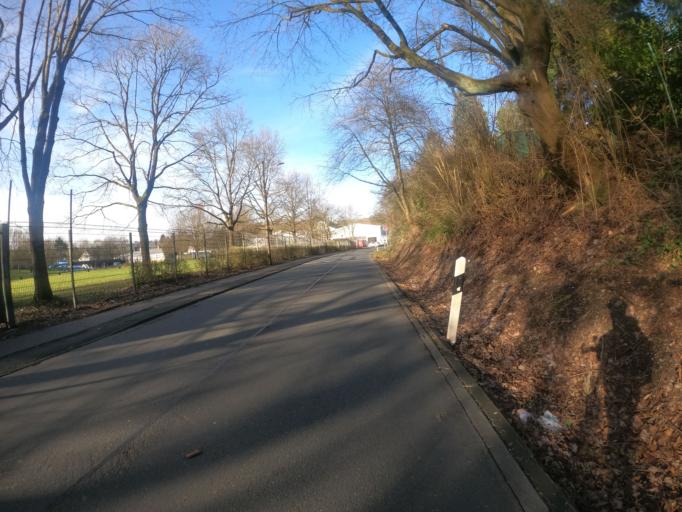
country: DE
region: North Rhine-Westphalia
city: Sprockhovel
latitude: 51.2917
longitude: 7.2332
